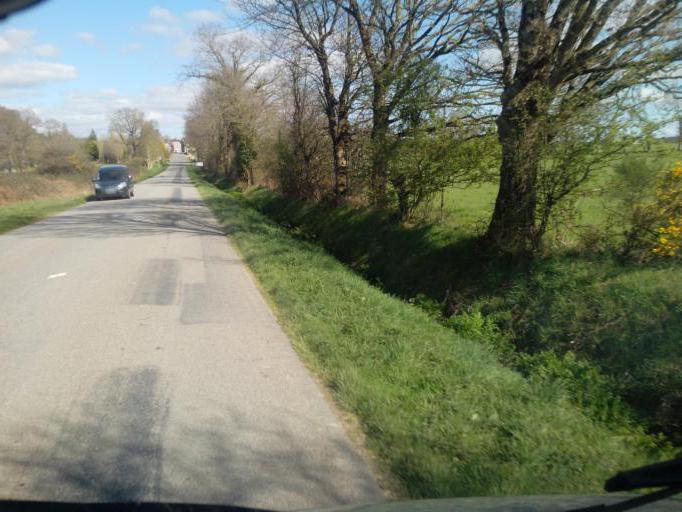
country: FR
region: Brittany
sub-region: Departement d'Ille-et-Vilaine
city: Paimpont
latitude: 48.0644
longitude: -2.2141
